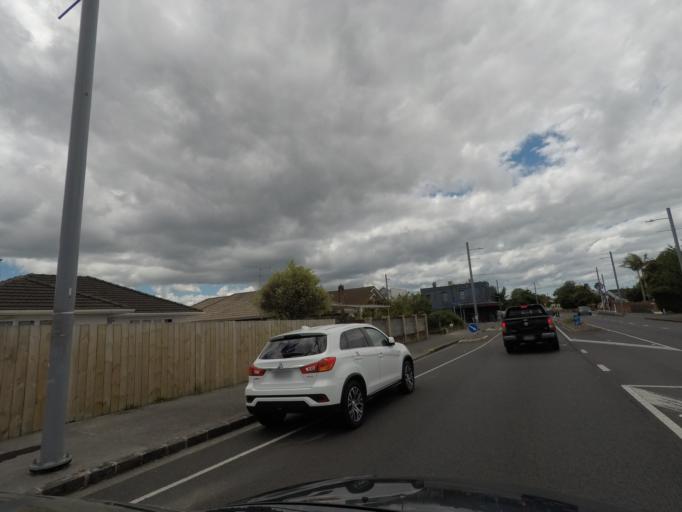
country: NZ
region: Auckland
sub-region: Auckland
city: Auckland
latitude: -36.8937
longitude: 174.7360
